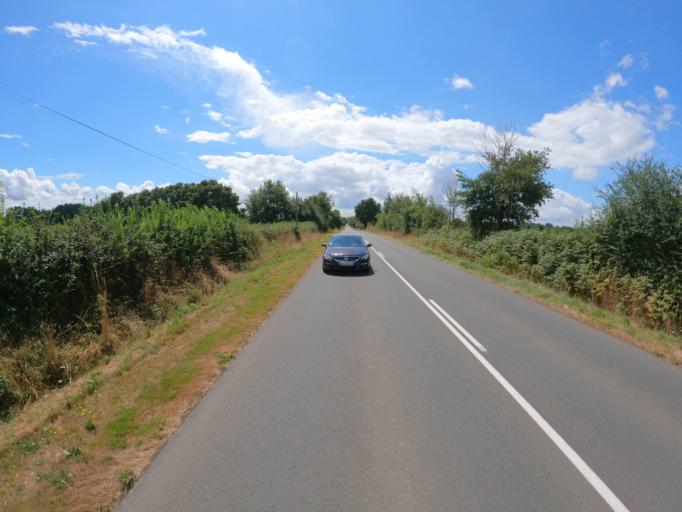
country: FR
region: Pays de la Loire
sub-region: Departement de Maine-et-Loire
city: Champigne
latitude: 47.6490
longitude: -0.5765
